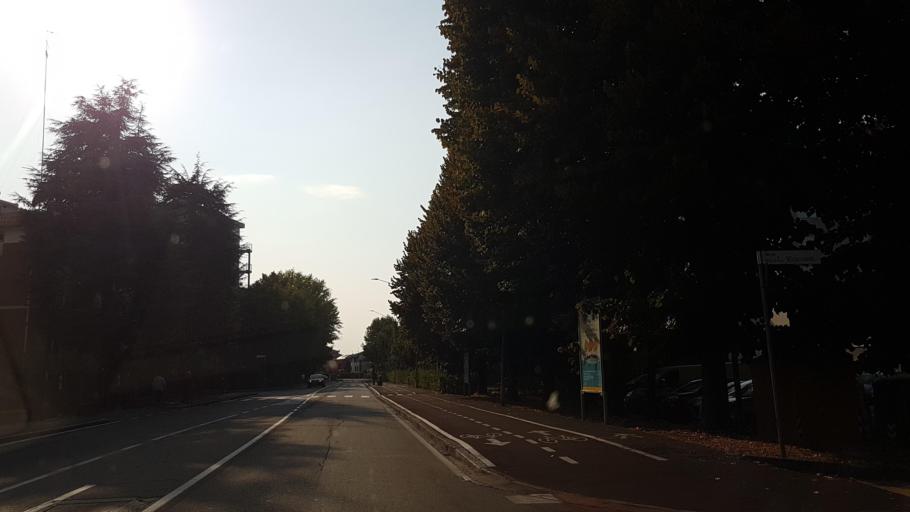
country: IT
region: Emilia-Romagna
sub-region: Provincia di Parma
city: Parma
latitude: 44.7966
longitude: 10.3028
